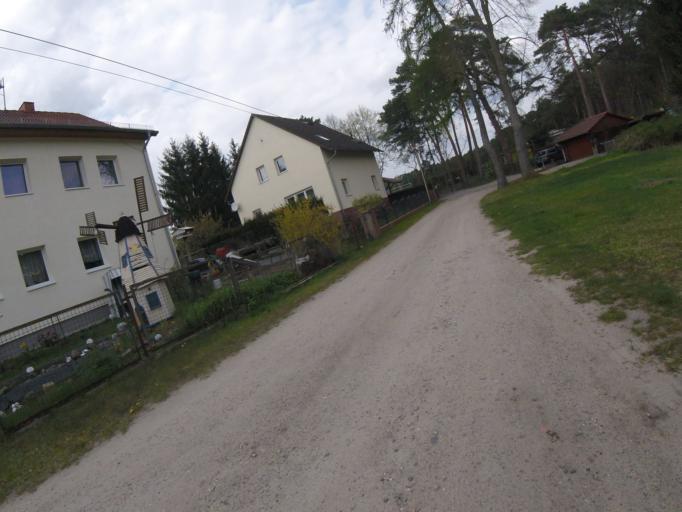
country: DE
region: Brandenburg
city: Gross Koris
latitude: 52.1713
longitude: 13.6589
